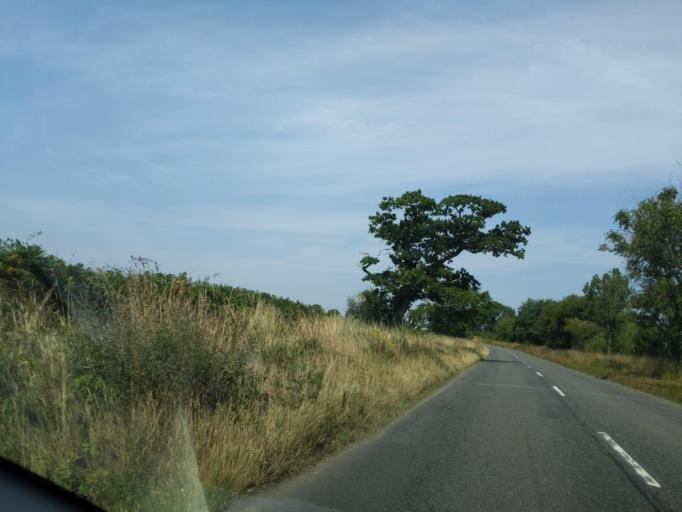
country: GB
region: England
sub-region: Devon
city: Okehampton
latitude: 50.7821
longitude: -4.0193
